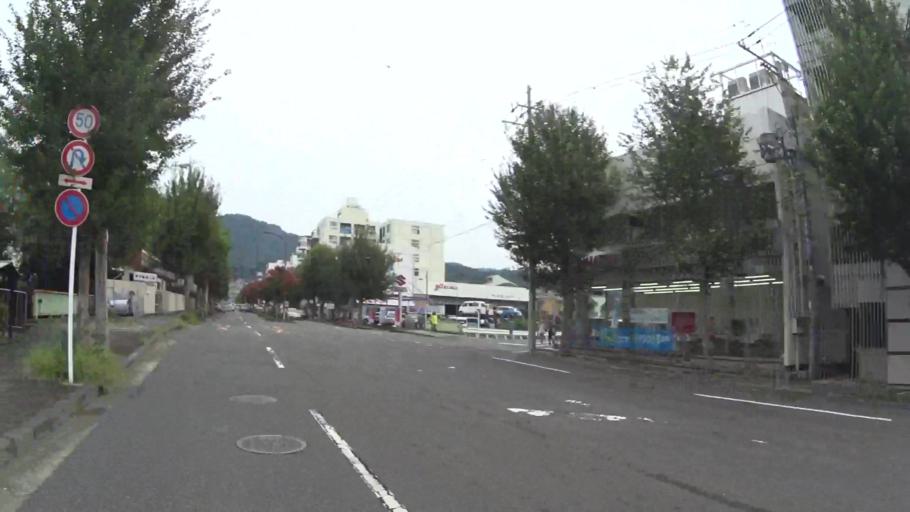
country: JP
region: Kyoto
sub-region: Kyoto-shi
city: Kamigyo-ku
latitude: 35.0405
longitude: 135.7856
